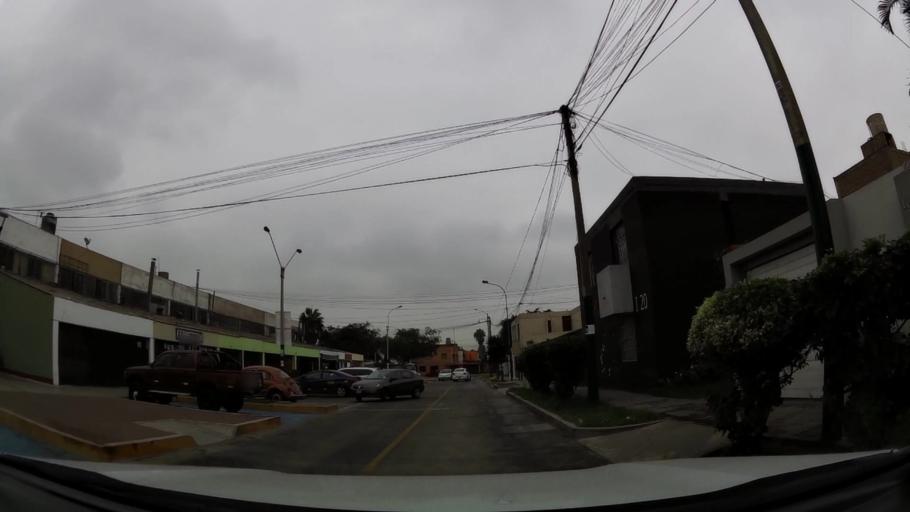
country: PE
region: Lima
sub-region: Lima
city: Surco
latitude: -12.1375
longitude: -77.0016
